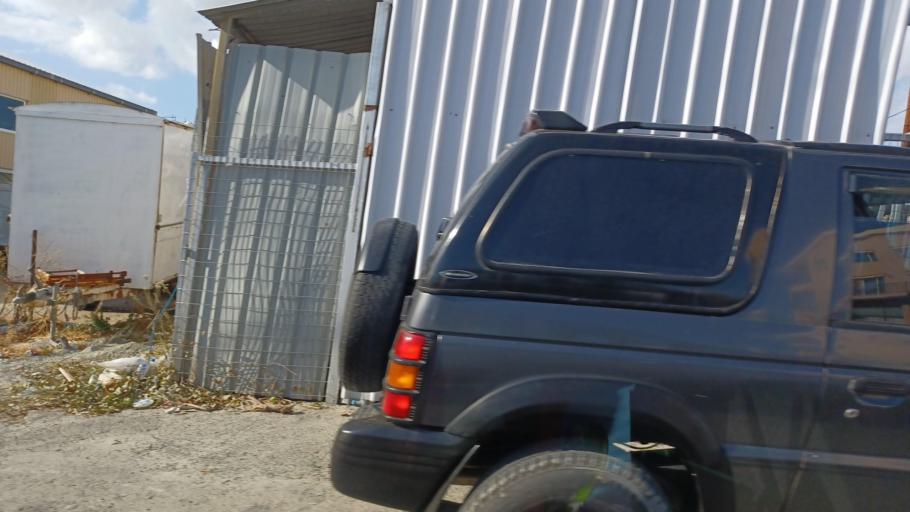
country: CY
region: Limassol
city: Limassol
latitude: 34.6772
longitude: 33.0080
